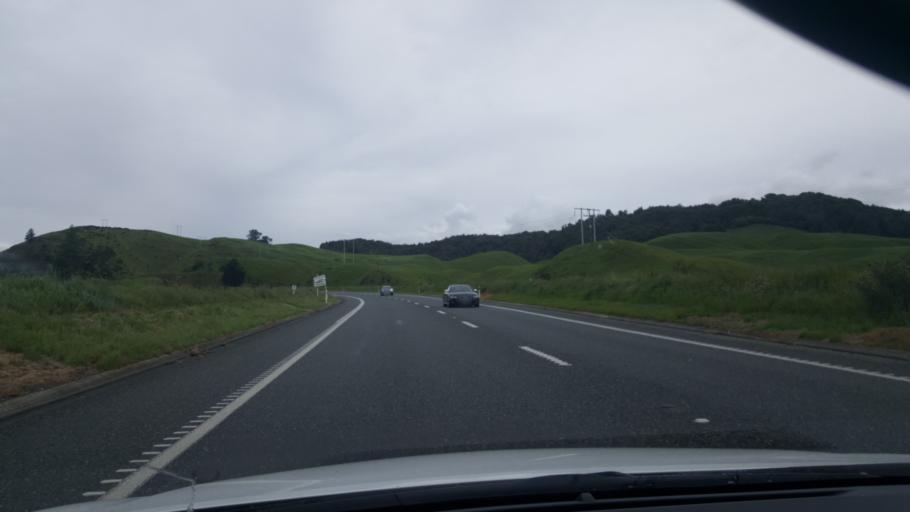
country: NZ
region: Bay of Plenty
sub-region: Rotorua District
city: Rotorua
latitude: -38.2605
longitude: 176.3201
